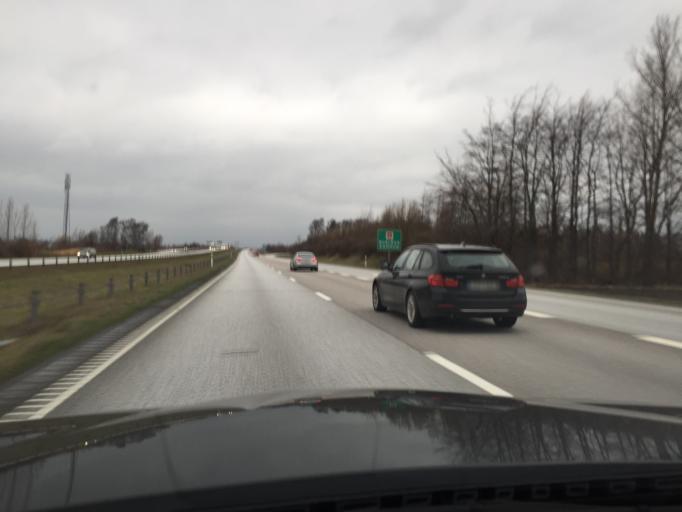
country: SE
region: Skane
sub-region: Burlovs Kommun
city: Arloev
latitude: 55.6071
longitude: 13.1163
